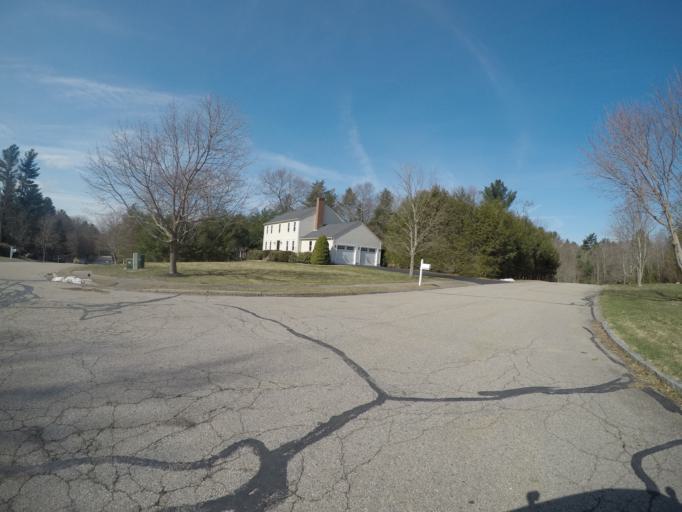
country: US
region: Massachusetts
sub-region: Bristol County
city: Easton
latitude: 42.0176
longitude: -71.1625
